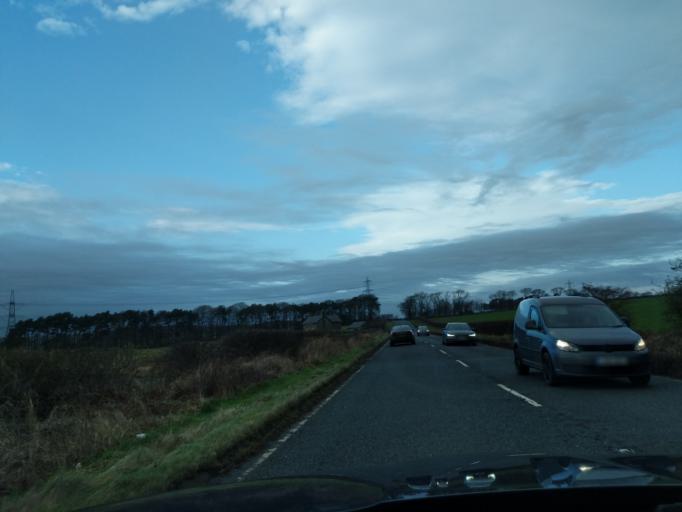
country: GB
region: England
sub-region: Northumberland
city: Meldon
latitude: 55.0988
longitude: -1.8219
